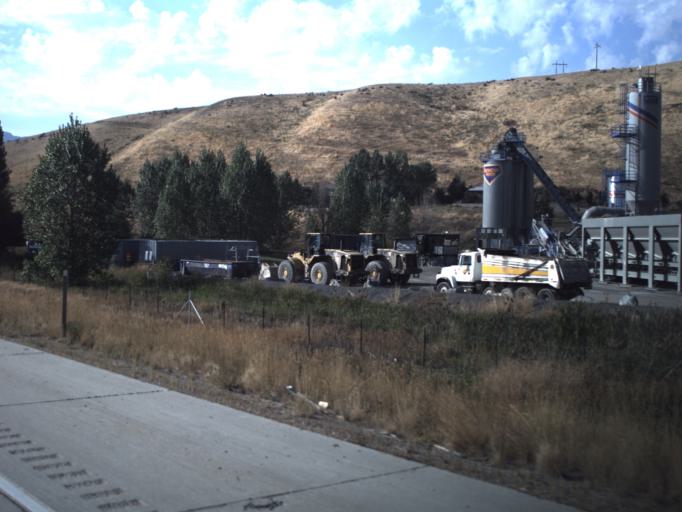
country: US
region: Utah
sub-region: Morgan County
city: Mountain Green
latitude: 41.1107
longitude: -111.7529
